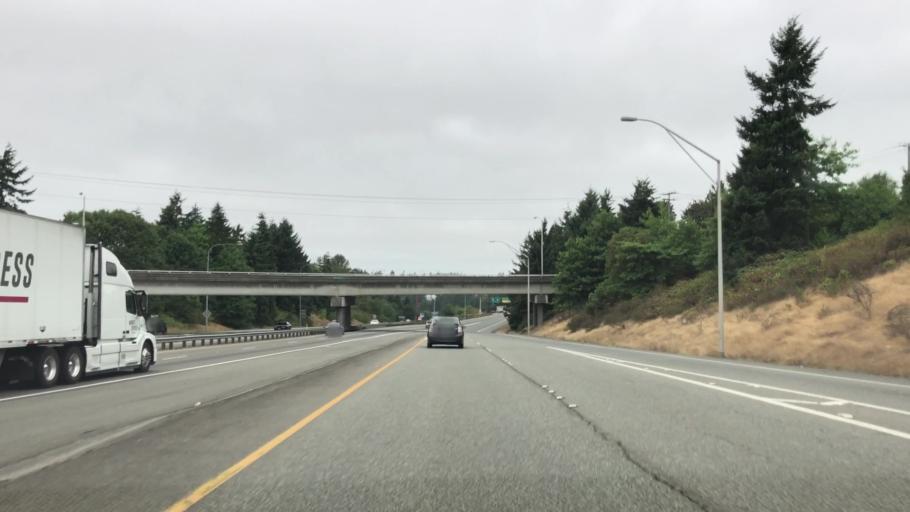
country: US
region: Washington
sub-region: King County
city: Riverton
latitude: 47.4660
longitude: -122.3010
